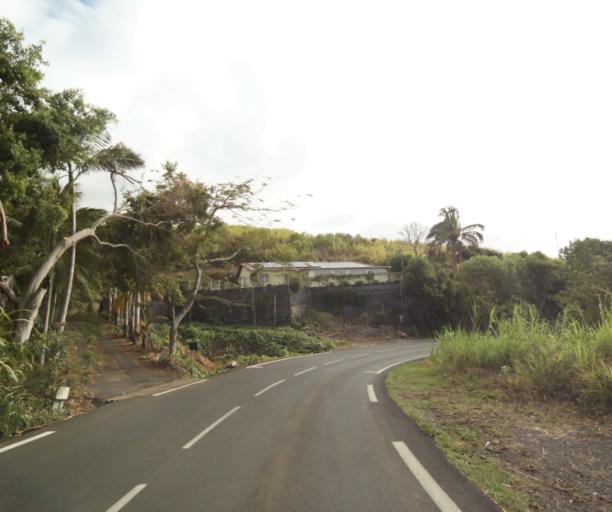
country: RE
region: Reunion
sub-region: Reunion
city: Saint-Paul
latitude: -21.0188
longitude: 55.3165
